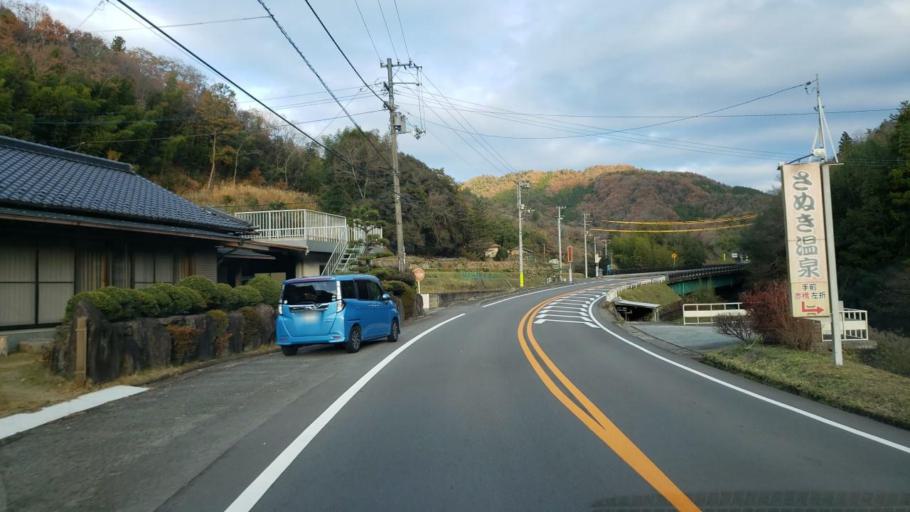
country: JP
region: Tokushima
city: Wakimachi
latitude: 34.1719
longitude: 134.0972
